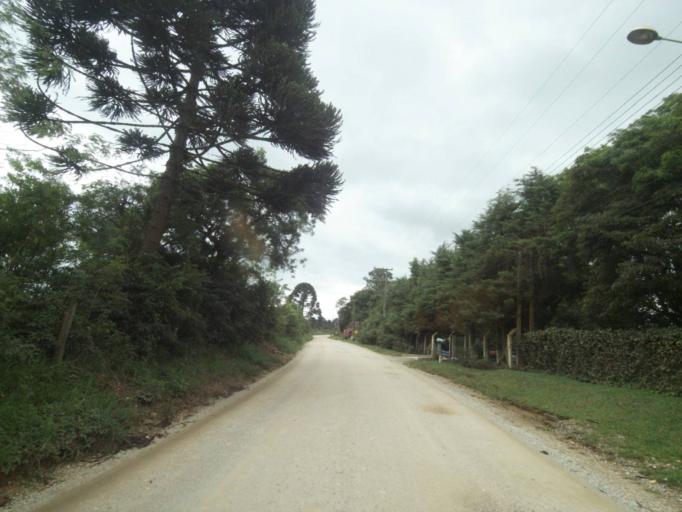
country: BR
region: Parana
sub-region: Campina Grande Do Sul
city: Campina Grande do Sul
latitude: -25.3236
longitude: -49.0842
